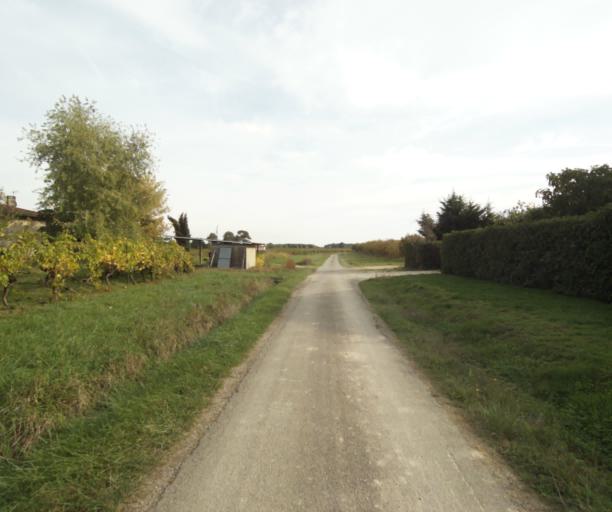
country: FR
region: Midi-Pyrenees
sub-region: Departement du Tarn-et-Garonne
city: Campsas
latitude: 43.9055
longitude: 1.3351
